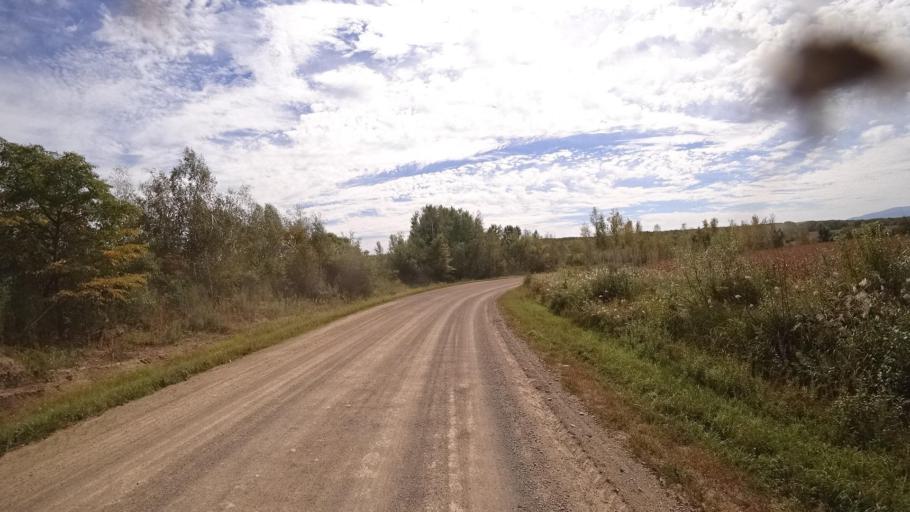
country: RU
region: Primorskiy
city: Yakovlevka
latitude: 44.5628
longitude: 133.5960
